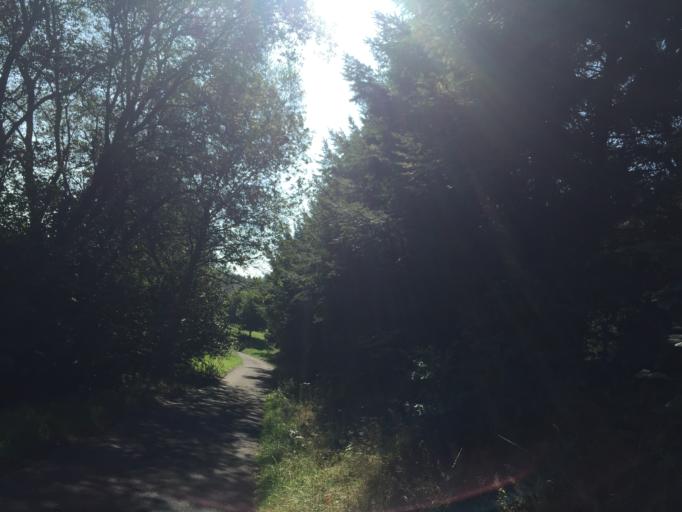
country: DE
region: Hesse
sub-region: Regierungsbezirk Darmstadt
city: Butzbach
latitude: 50.4388
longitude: 8.5823
